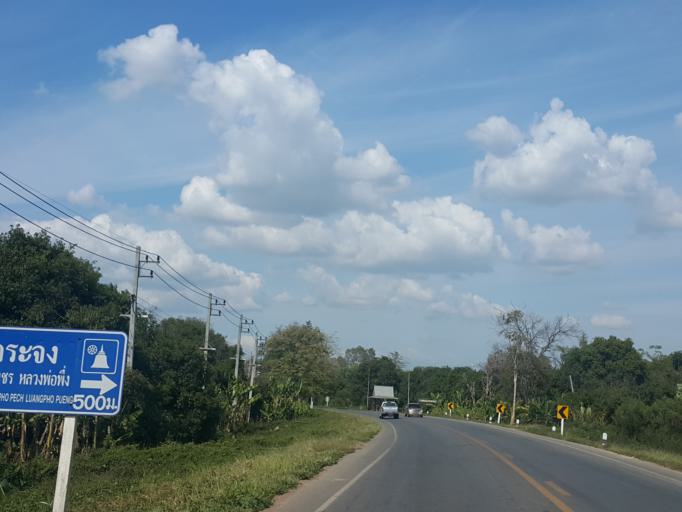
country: TH
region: Sukhothai
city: Sawankhalok
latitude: 17.2438
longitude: 99.8472
